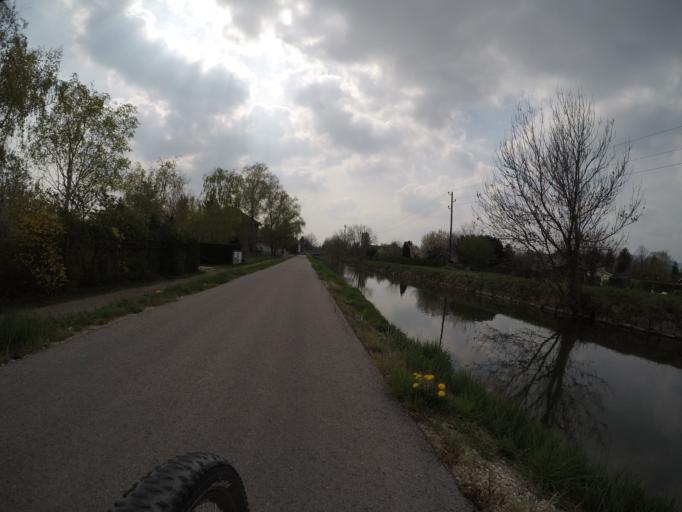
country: AT
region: Lower Austria
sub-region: Politischer Bezirk Baden
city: Pfaffstatten
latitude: 48.0018
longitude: 16.2607
